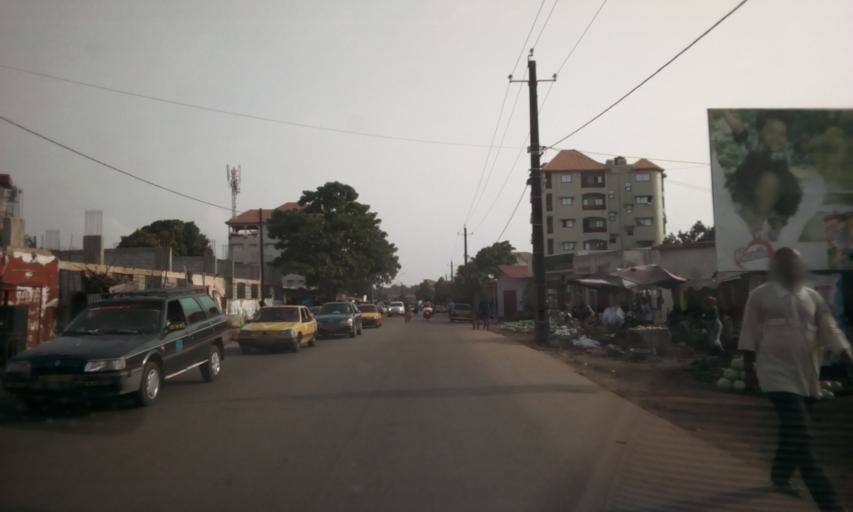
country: GN
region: Conakry
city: Conakry
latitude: 9.6123
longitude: -13.6446
